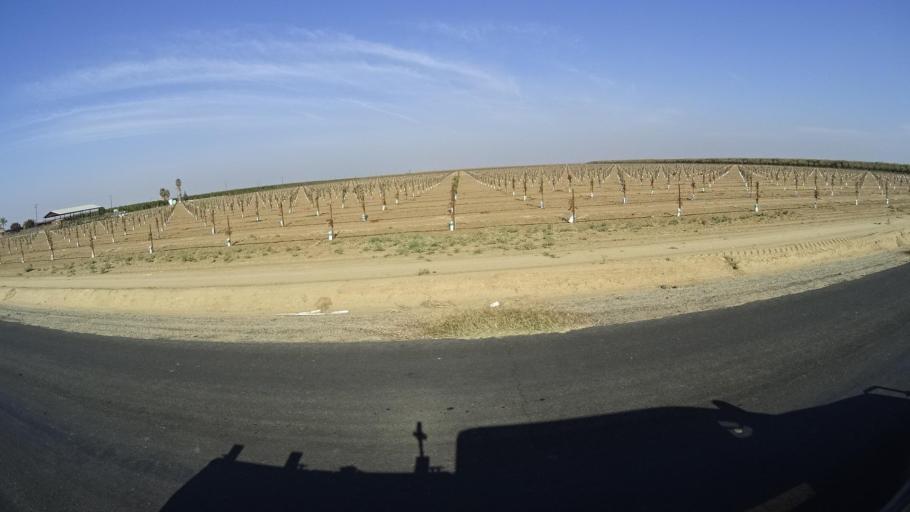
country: US
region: California
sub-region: Kern County
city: McFarland
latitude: 35.6746
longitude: -119.1675
